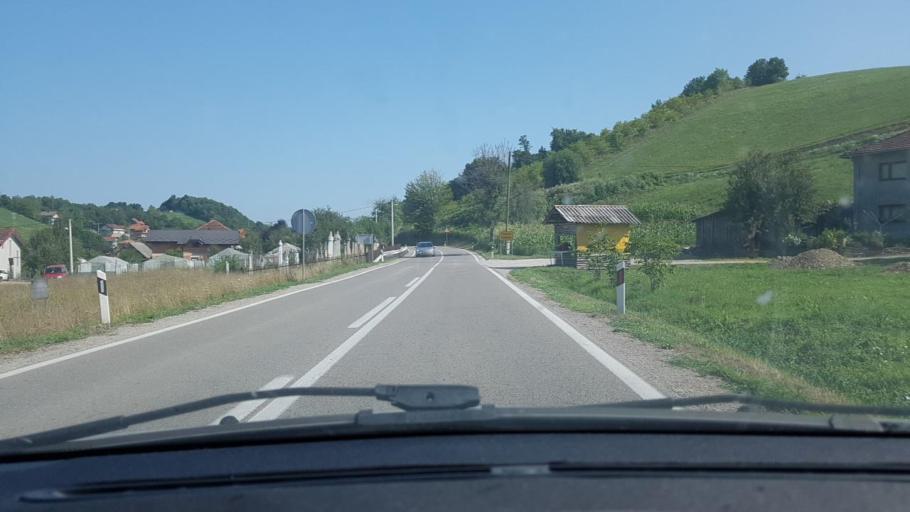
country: BA
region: Federation of Bosnia and Herzegovina
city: Pecigrad
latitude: 45.0704
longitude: 15.8894
